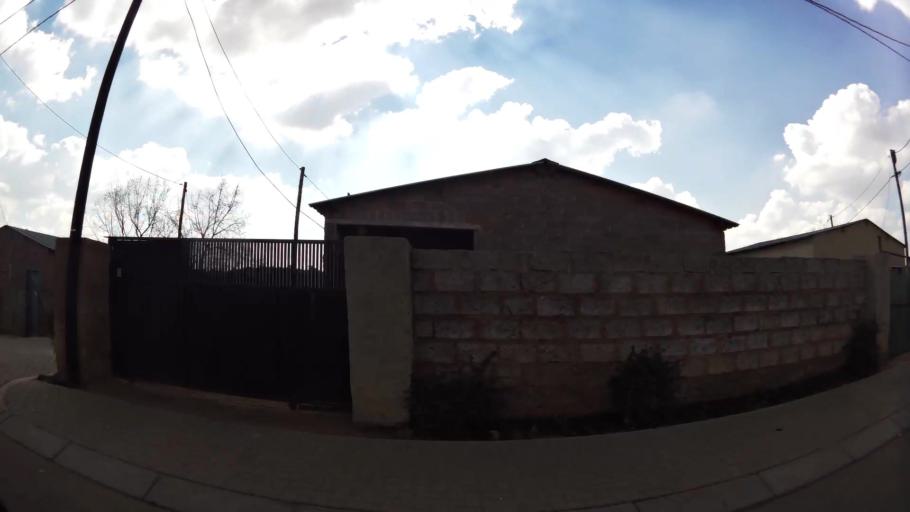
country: ZA
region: Gauteng
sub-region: City of Johannesburg Metropolitan Municipality
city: Roodepoort
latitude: -26.1819
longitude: 27.8552
